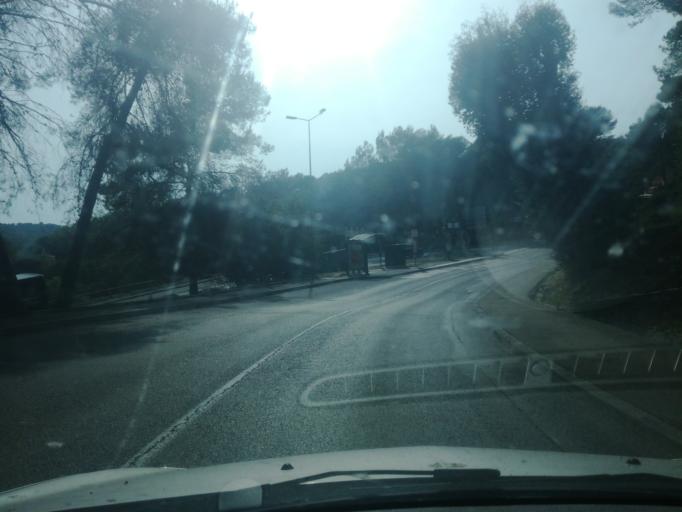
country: FR
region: Provence-Alpes-Cote d'Azur
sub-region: Departement des Alpes-Maritimes
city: Vallauris
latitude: 43.6140
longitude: 7.0568
